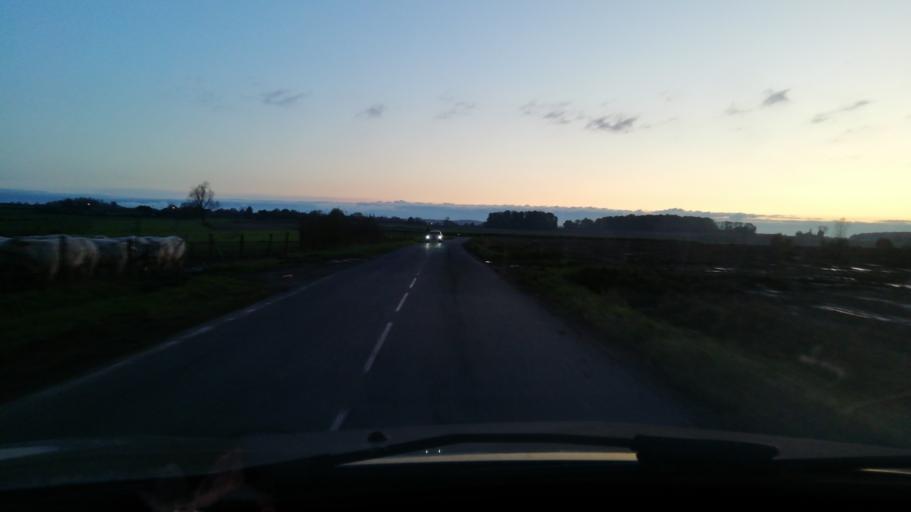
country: FR
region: Nord-Pas-de-Calais
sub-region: Departement du Nord
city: Marpent
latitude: 50.2744
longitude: 4.0883
